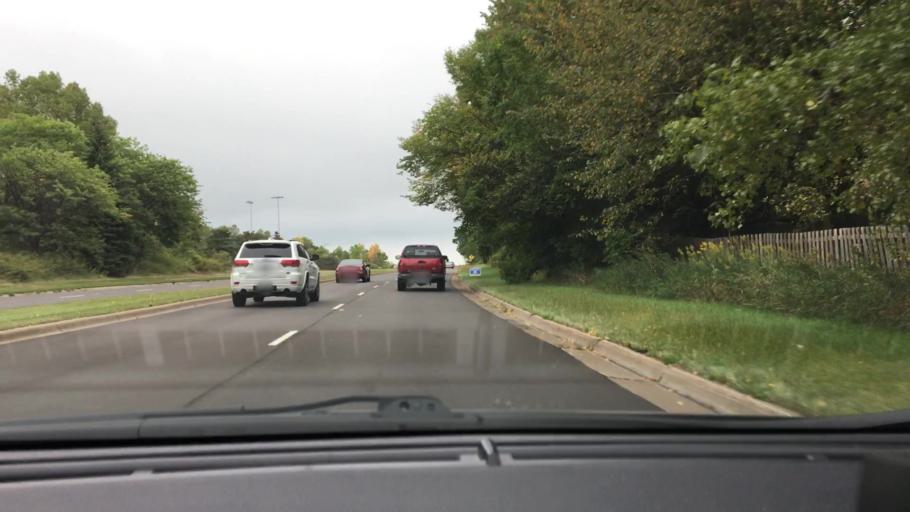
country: US
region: Minnesota
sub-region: Hennepin County
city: Plymouth
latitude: 45.0335
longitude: -93.4270
